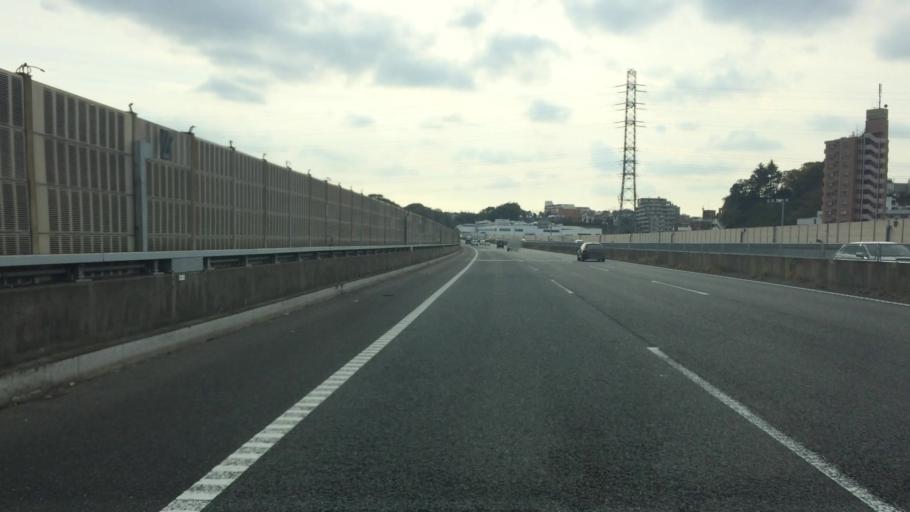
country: JP
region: Tokyo
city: Chofugaoka
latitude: 35.5878
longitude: 139.6216
